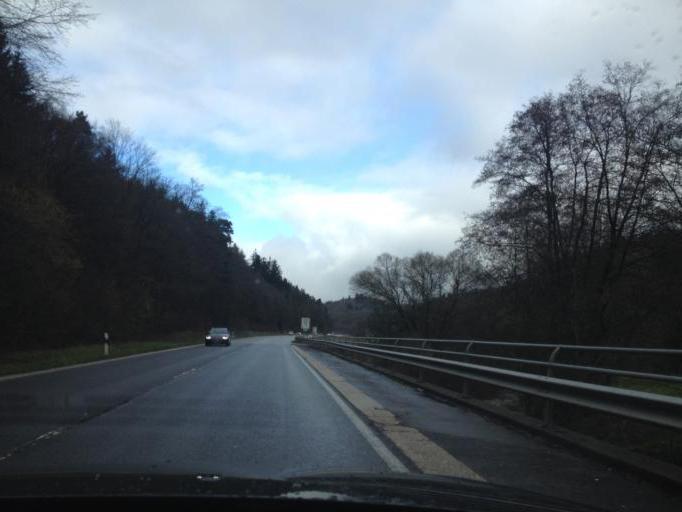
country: DE
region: Rheinland-Pfalz
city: Ellweiler
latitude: 49.6231
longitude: 7.1597
